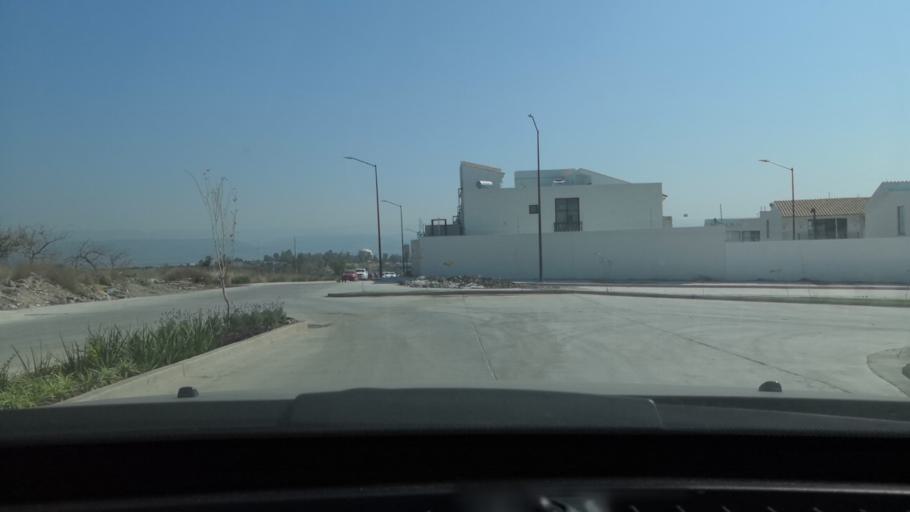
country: MX
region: Guanajuato
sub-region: Leon
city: La Ermita
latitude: 21.1633
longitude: -101.7379
